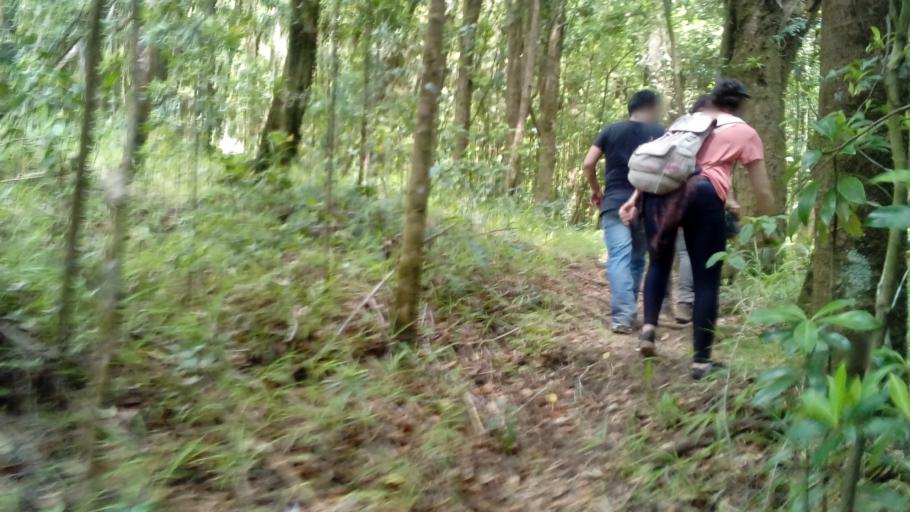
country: CR
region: Alajuela
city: Sabanilla
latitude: 10.1578
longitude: -84.2397
